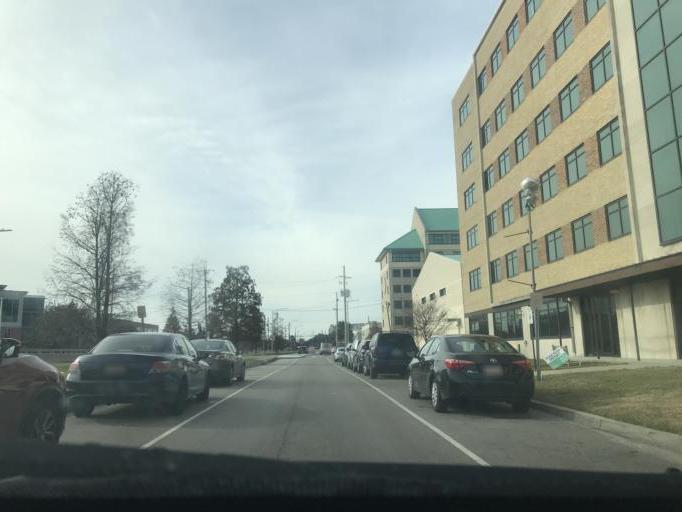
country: US
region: Louisiana
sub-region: Orleans Parish
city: New Orleans
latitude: 29.9616
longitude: -90.1018
